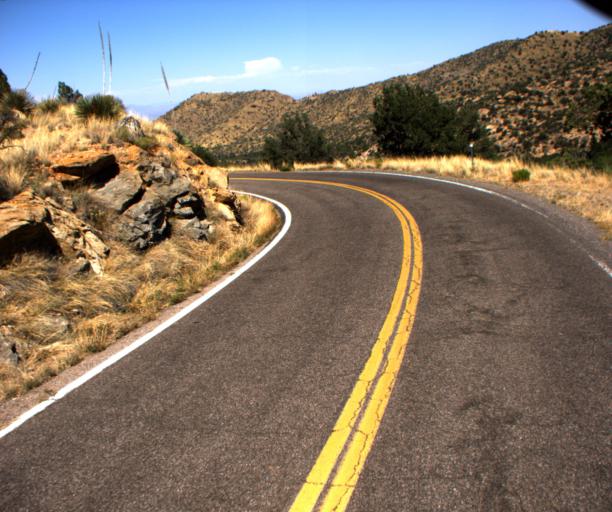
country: US
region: Arizona
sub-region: Graham County
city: Swift Trail Junction
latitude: 32.6690
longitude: -109.7898
